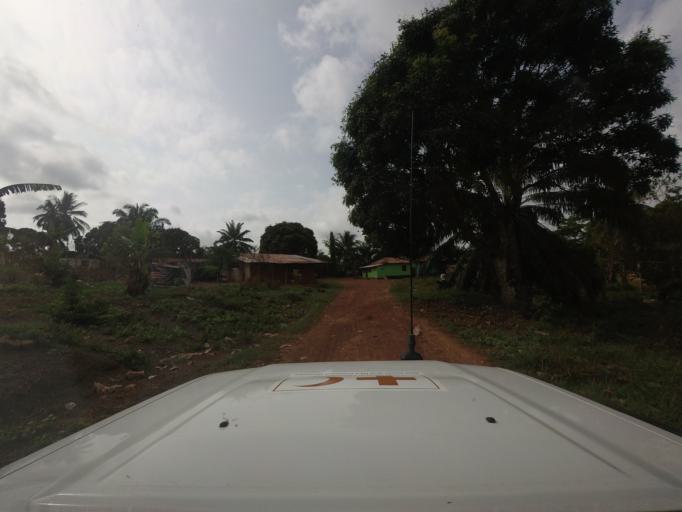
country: LR
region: Bong
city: Gbarnga
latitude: 7.0046
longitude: -9.4743
